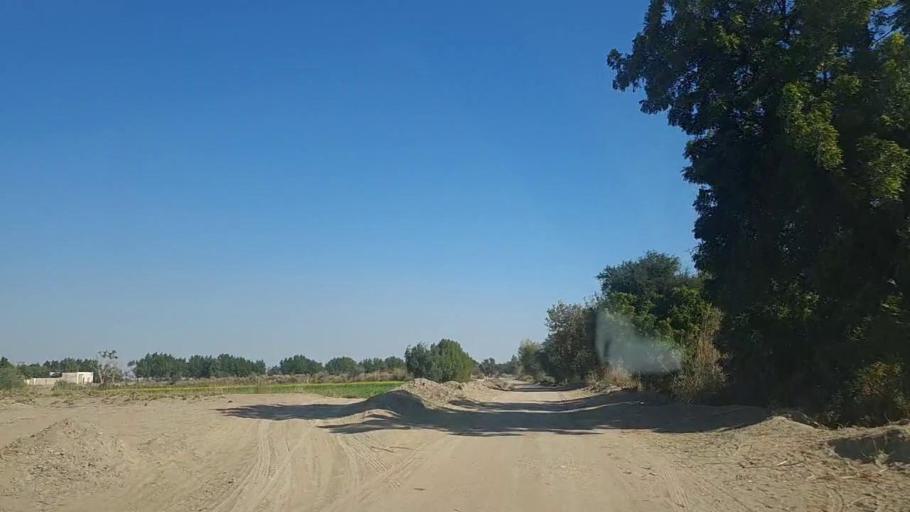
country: PK
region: Sindh
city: Sanghar
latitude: 26.2091
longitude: 68.9070
